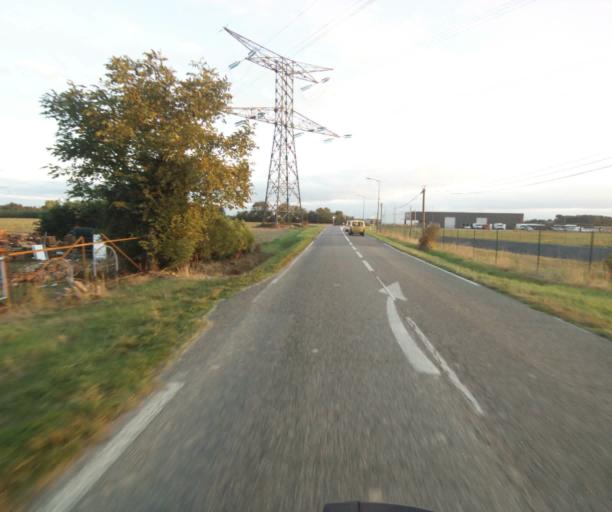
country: FR
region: Midi-Pyrenees
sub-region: Departement du Tarn-et-Garonne
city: Verdun-sur-Garonne
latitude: 43.8239
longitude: 1.2444
